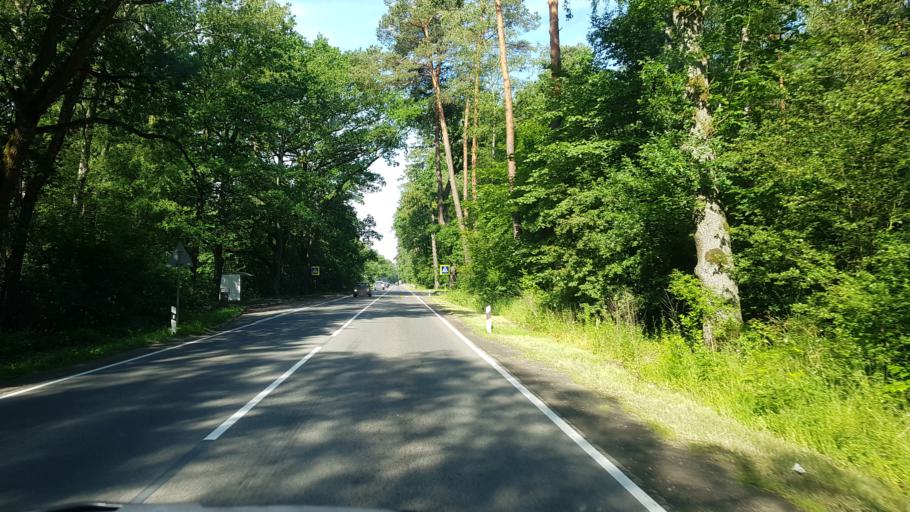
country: RU
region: Kaliningrad
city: Vzmorye
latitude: 54.7047
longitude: 20.2999
